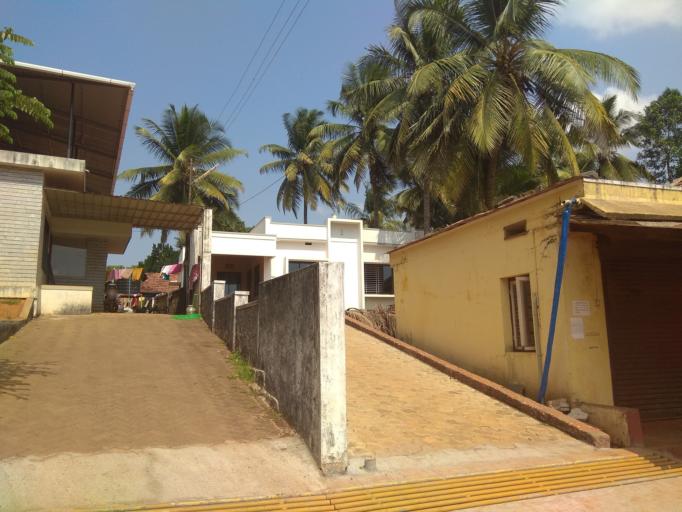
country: IN
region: Karnataka
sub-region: Dakshina Kannada
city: Mangalore
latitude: 12.9469
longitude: 74.8472
